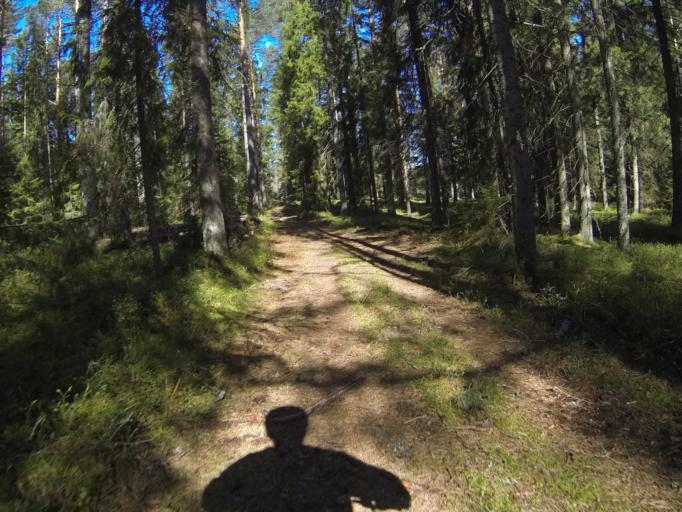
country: FI
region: Varsinais-Suomi
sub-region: Salo
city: Pertteli
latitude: 60.3929
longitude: 23.2187
